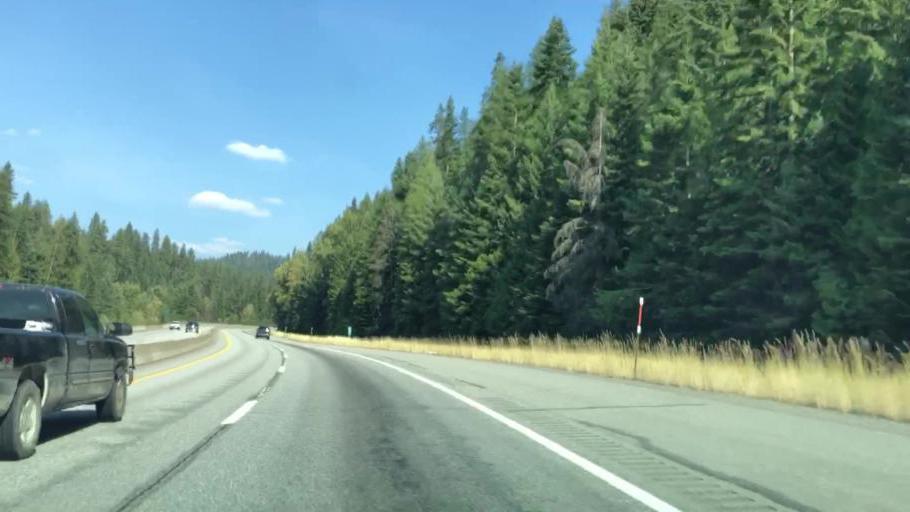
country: US
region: Idaho
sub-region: Kootenai County
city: Coeur d'Alene
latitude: 47.6224
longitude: -116.5536
